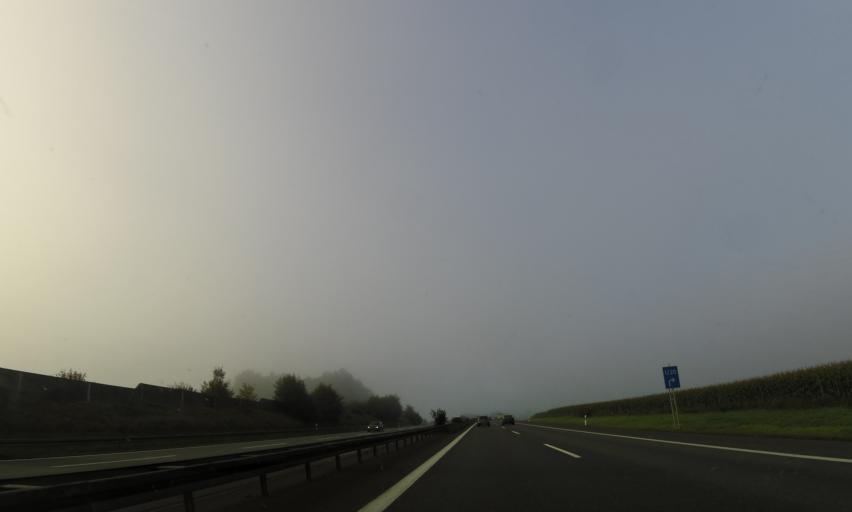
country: DE
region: Saxony
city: Neuensalz
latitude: 50.5099
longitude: 12.2190
